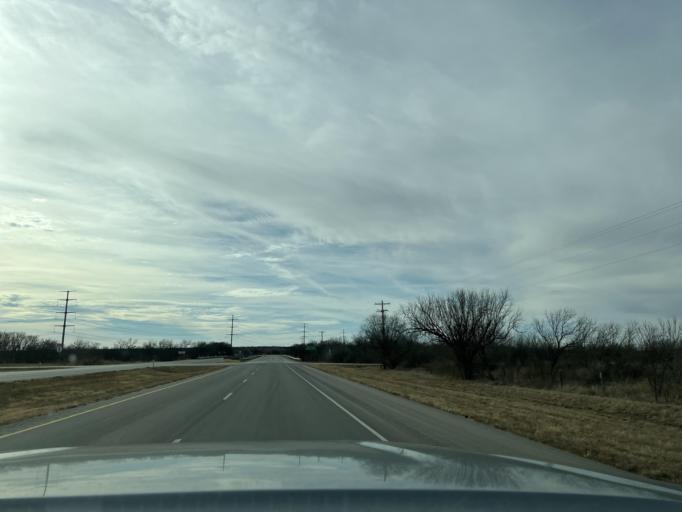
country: US
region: Texas
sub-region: Jones County
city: Stamford
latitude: 32.7528
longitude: -99.6226
